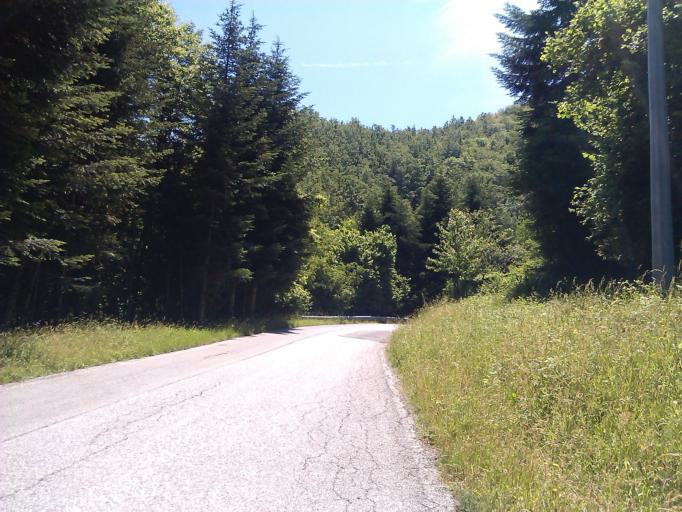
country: IT
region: Tuscany
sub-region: Provincia di Prato
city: Cantagallo
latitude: 44.0532
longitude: 11.0451
